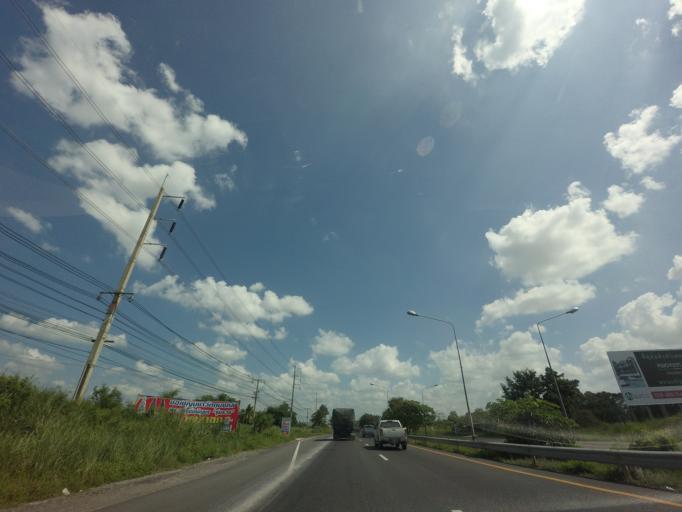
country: TH
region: Chon Buri
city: Ban Bueng
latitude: 13.2957
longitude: 101.1639
